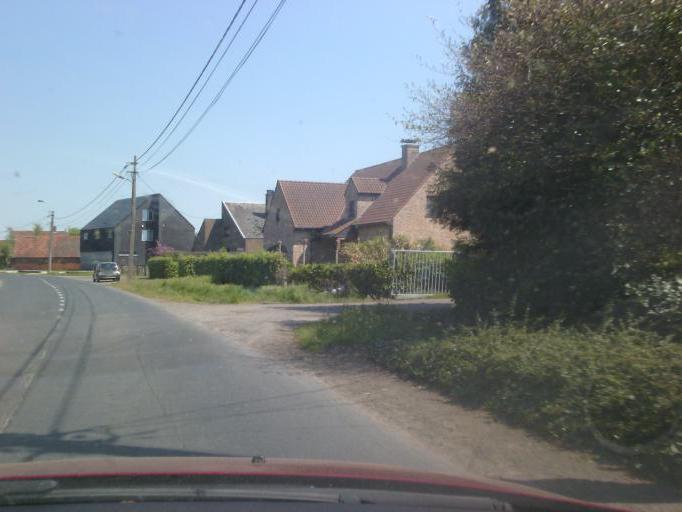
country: BE
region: Flanders
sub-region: Provincie Oost-Vlaanderen
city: Lokeren
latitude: 51.0879
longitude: 3.9674
